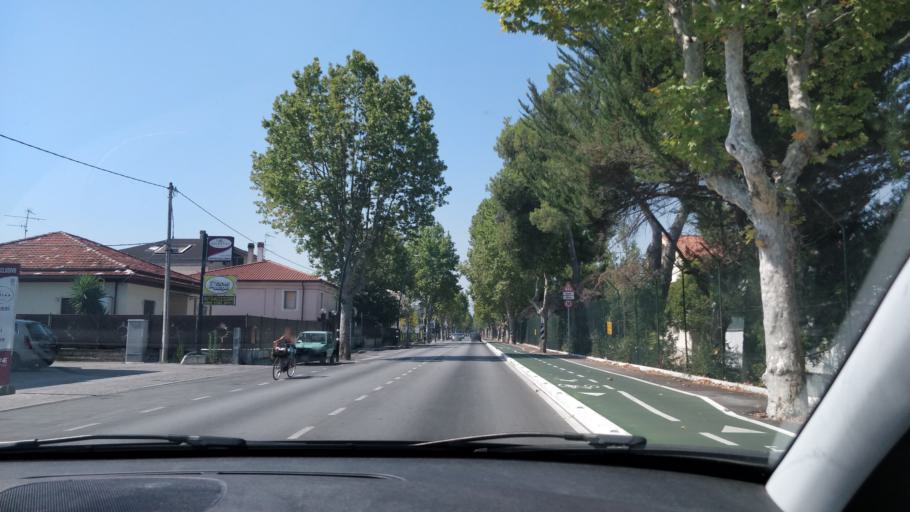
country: IT
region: Abruzzo
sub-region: Provincia di Chieti
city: Sambuceto
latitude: 42.4348
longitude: 14.1926
